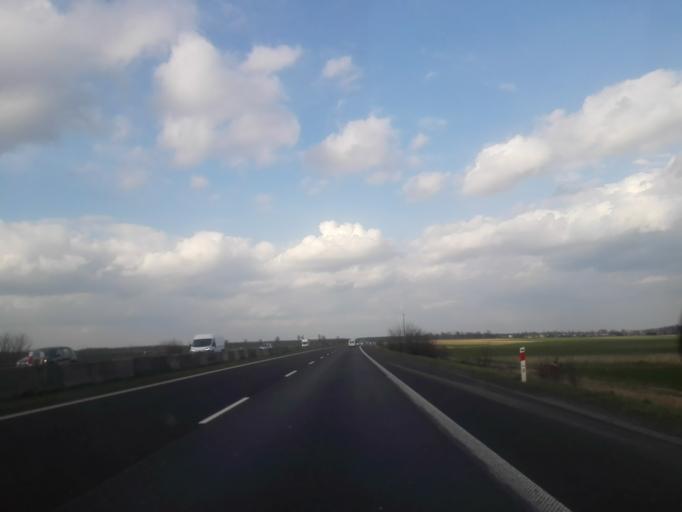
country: PL
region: Silesian Voivodeship
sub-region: Powiat czestochowski
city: Borowno
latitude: 50.9581
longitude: 19.2503
